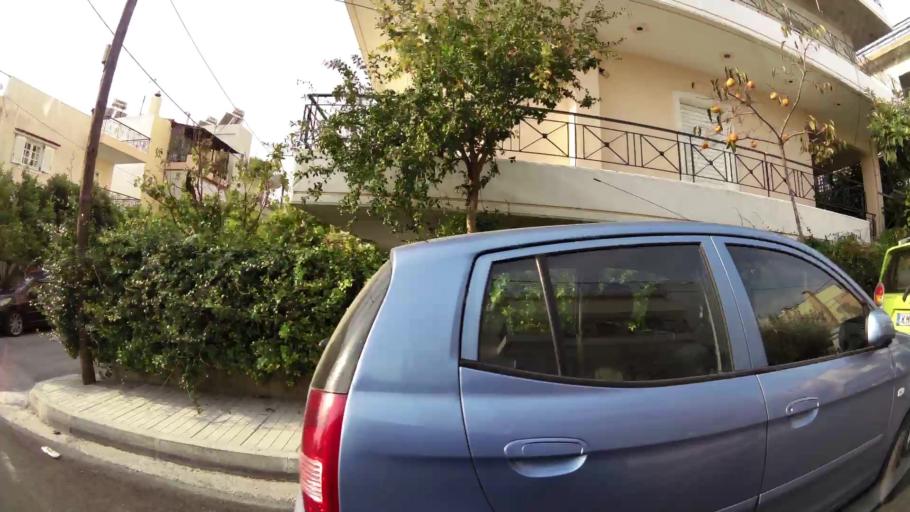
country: GR
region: Attica
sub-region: Nomarchia Athinas
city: Kamateron
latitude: 38.0540
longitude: 23.6967
